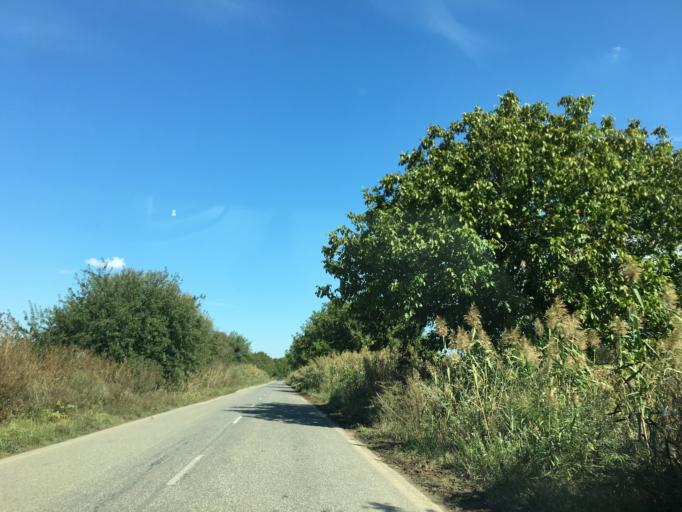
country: RO
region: Olt
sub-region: Comuna Orlea
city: Orlea
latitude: 43.6144
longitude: 24.3686
